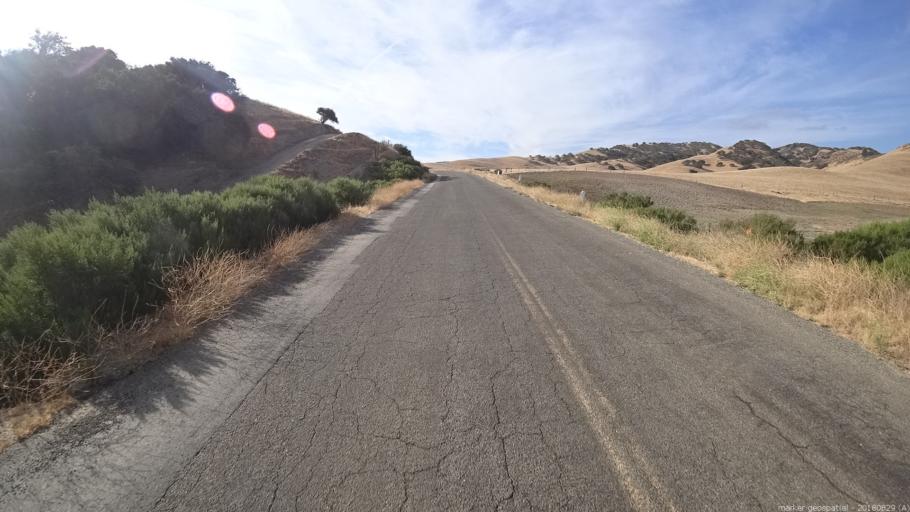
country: US
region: California
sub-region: Monterey County
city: King City
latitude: 36.0313
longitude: -120.9609
